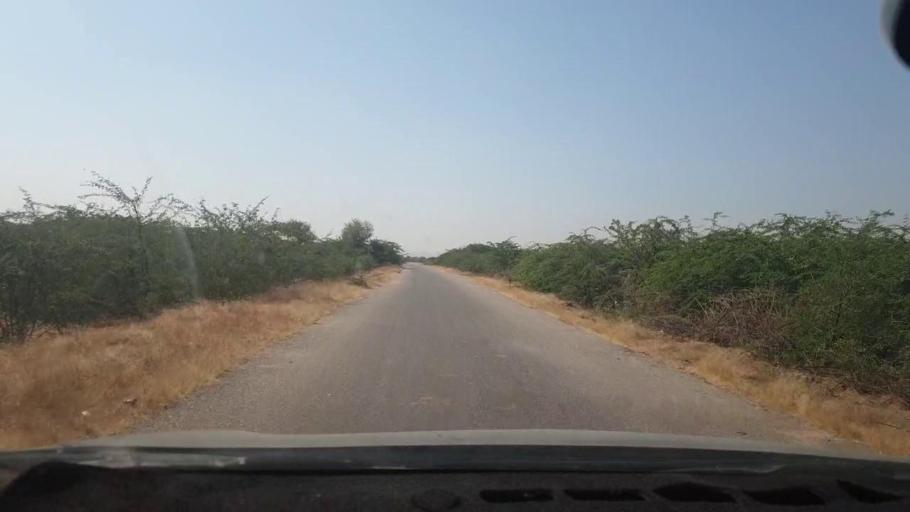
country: PK
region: Sindh
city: Malir Cantonment
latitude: 25.1576
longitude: 67.1489
